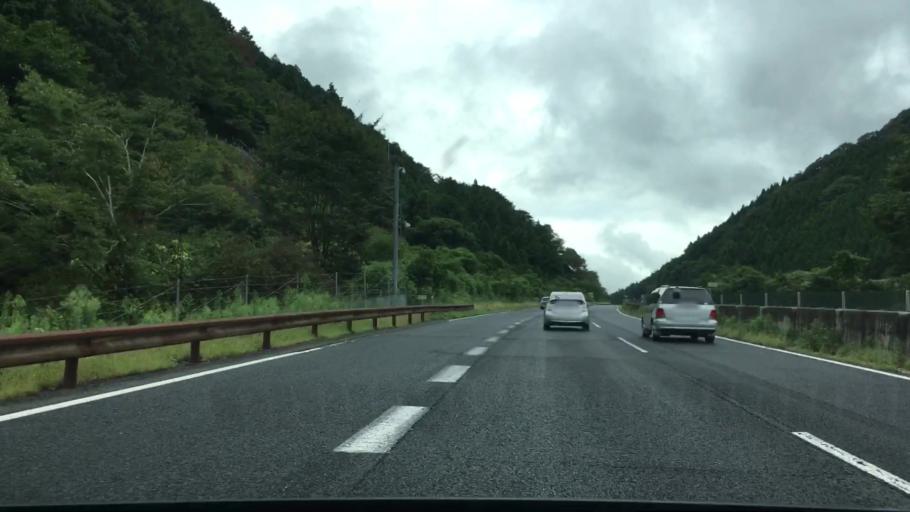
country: JP
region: Hyogo
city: Yamazakicho-nakabirose
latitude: 35.0389
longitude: 134.4715
